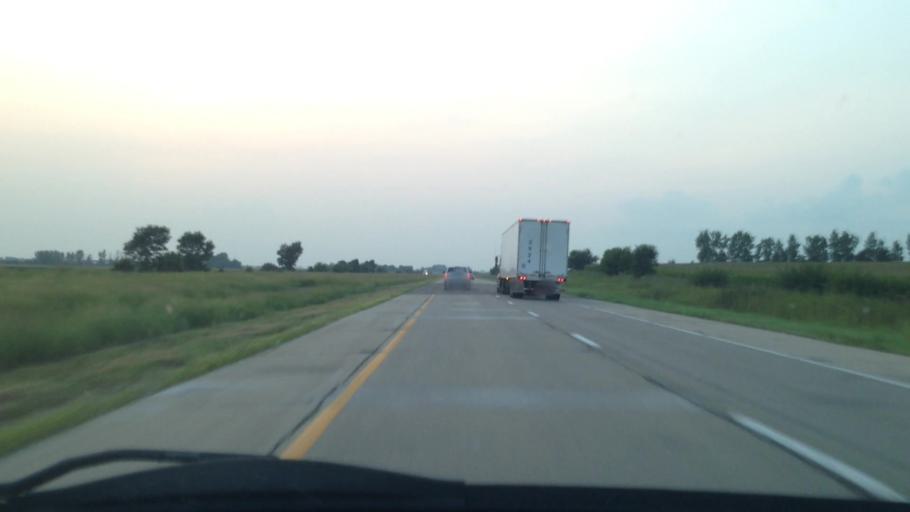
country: US
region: Iowa
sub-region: Benton County
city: Urbana
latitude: 42.2639
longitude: -91.9148
